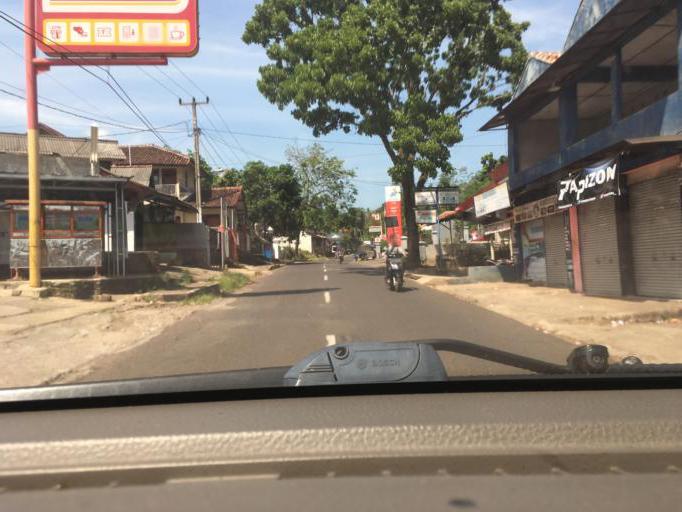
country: ID
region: West Java
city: Cilengkrang
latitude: -6.9542
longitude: 108.0951
